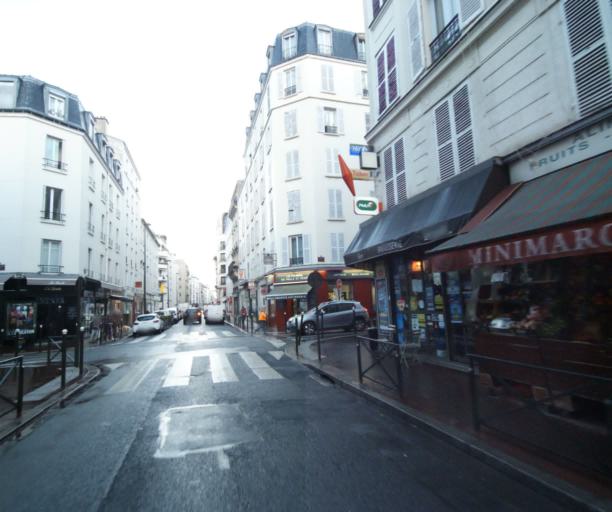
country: FR
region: Ile-de-France
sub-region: Departement des Hauts-de-Seine
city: Levallois-Perret
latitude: 48.8896
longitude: 2.2841
